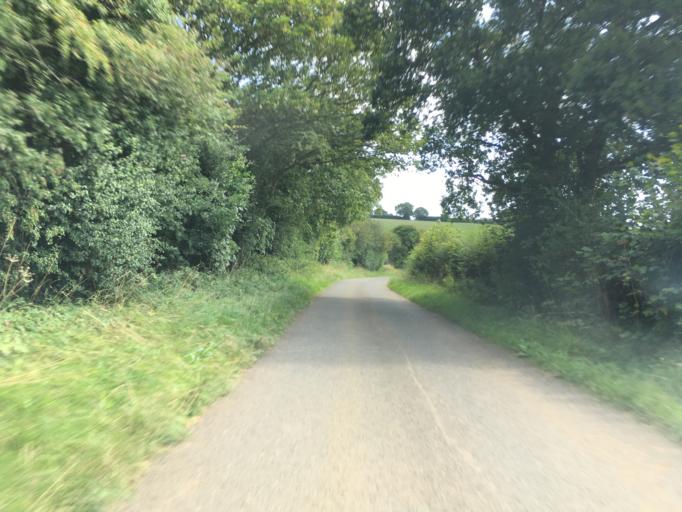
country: GB
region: England
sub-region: Wiltshire
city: Luckington
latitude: 51.6098
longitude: -2.2520
